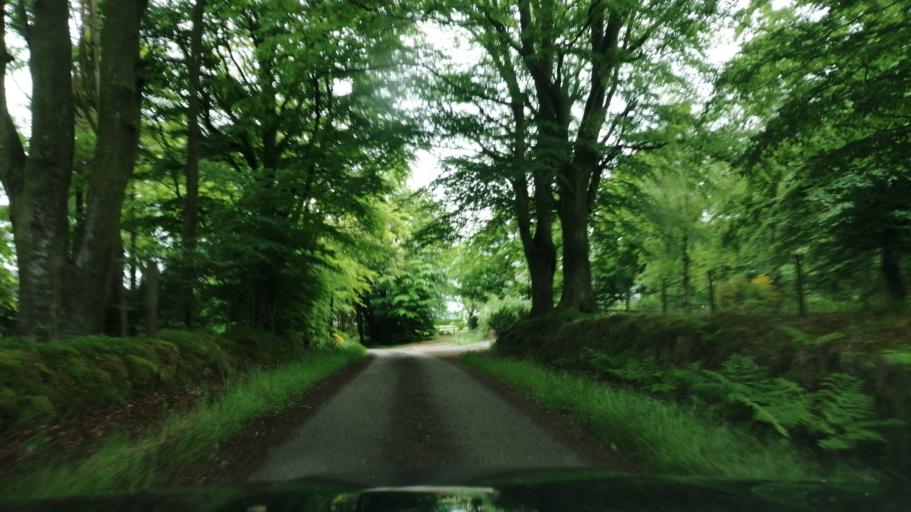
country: GB
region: Scotland
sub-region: Moray
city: Keith
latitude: 57.5571
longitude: -2.8653
